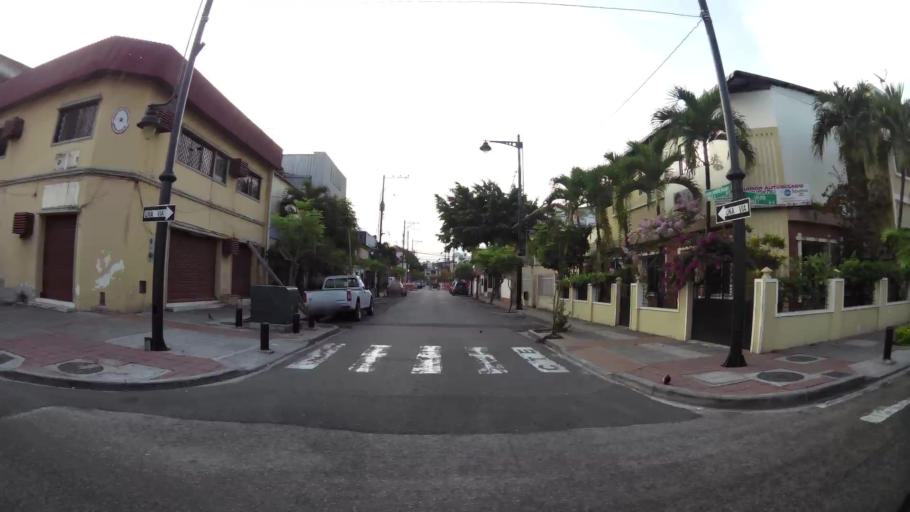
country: EC
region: Guayas
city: Guayaquil
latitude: -2.1858
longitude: -79.8933
